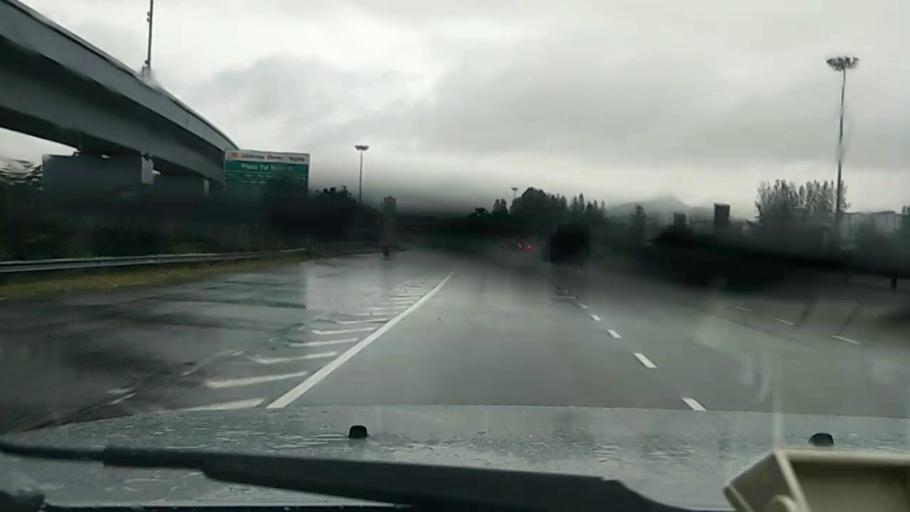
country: MY
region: Selangor
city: Kampong Baharu Balakong
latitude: 3.0443
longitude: 101.7749
